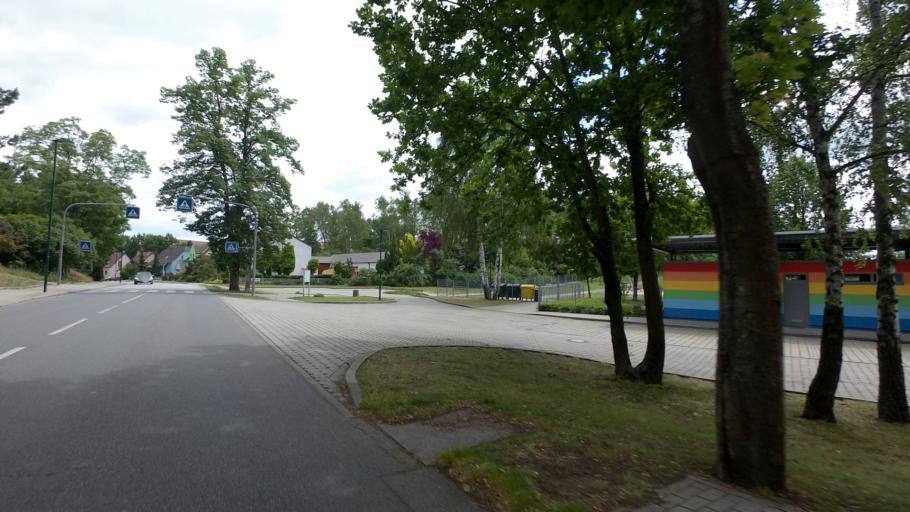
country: DE
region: Brandenburg
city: Luckau
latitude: 51.8518
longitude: 13.6973
